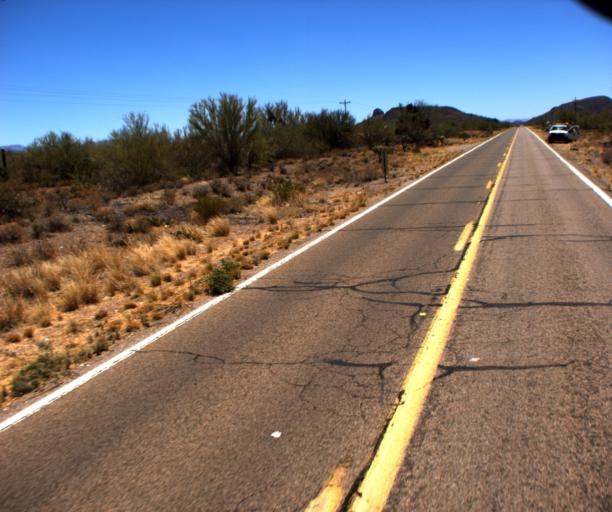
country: US
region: Arizona
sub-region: Pima County
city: Sells
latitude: 31.9827
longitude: -111.9711
